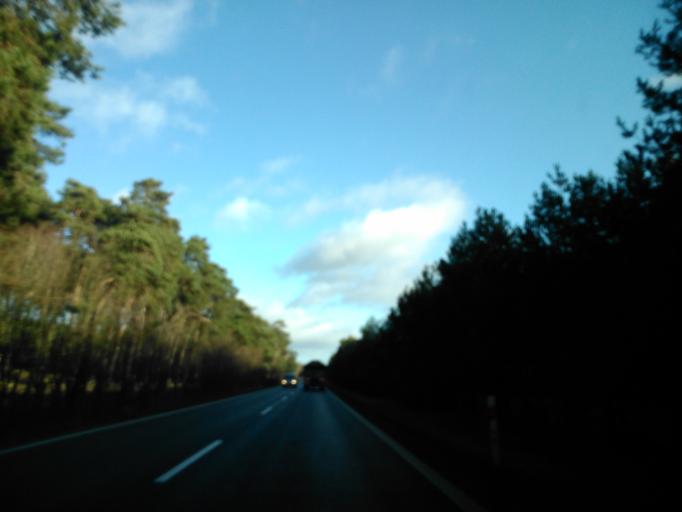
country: PL
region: Kujawsko-Pomorskie
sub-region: Powiat torunski
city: Wielka Nieszawka
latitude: 52.9280
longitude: 18.5053
